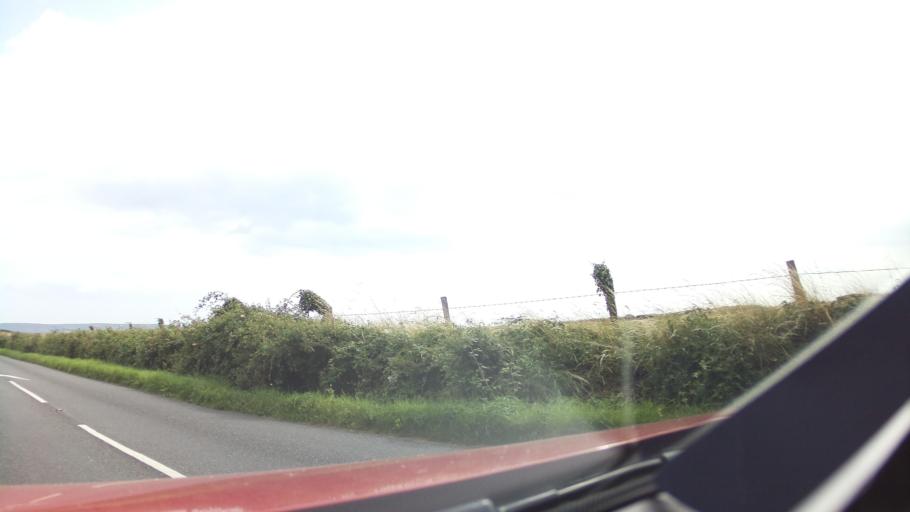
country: GB
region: England
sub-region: Hampshire
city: Milford on Sea
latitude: 50.7297
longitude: -1.6170
